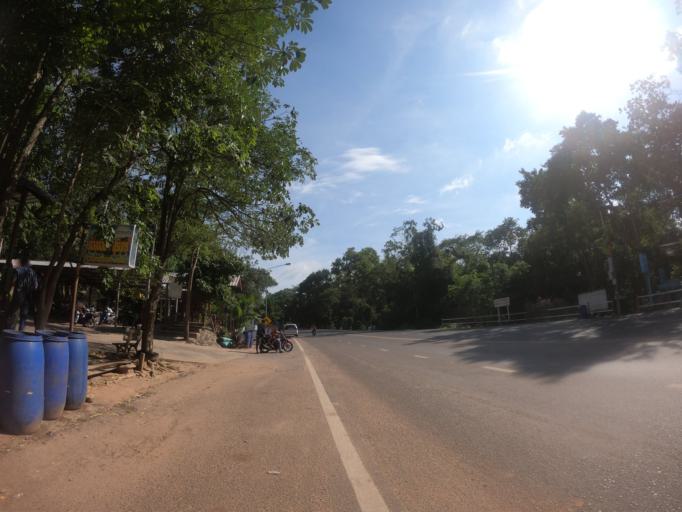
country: TH
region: Surin
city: Kap Choeng
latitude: 14.4360
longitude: 103.7005
